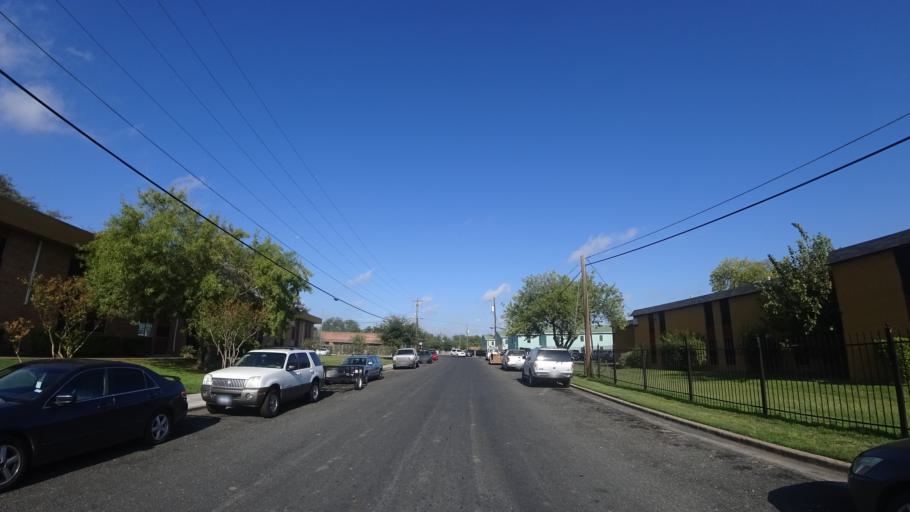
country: US
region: Texas
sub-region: Travis County
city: Austin
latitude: 30.3265
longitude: -97.6899
